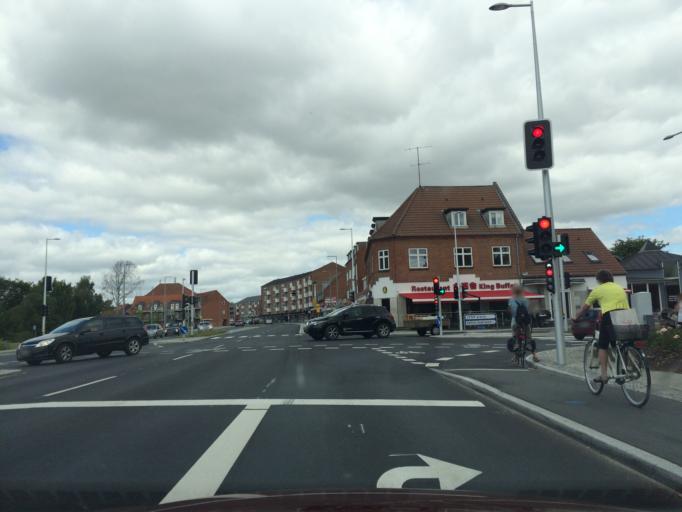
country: DK
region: Central Jutland
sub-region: Silkeborg Kommune
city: Silkeborg
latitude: 56.1755
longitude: 9.5553
